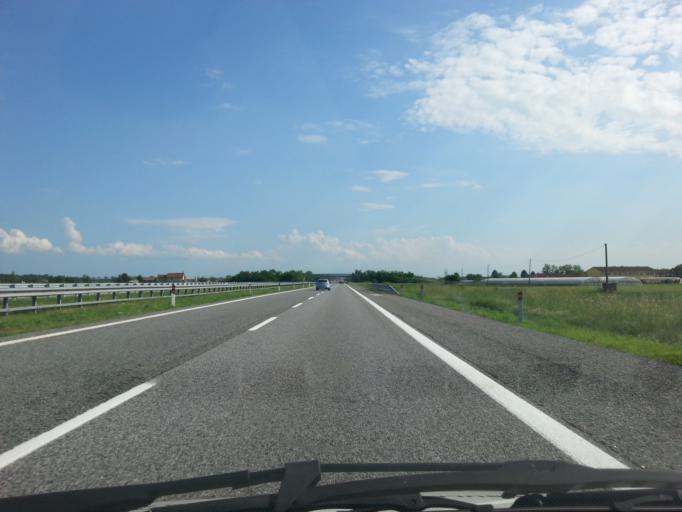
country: IT
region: Piedmont
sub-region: Provincia di Torino
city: Carmagnola
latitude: 44.8333
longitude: 7.7499
